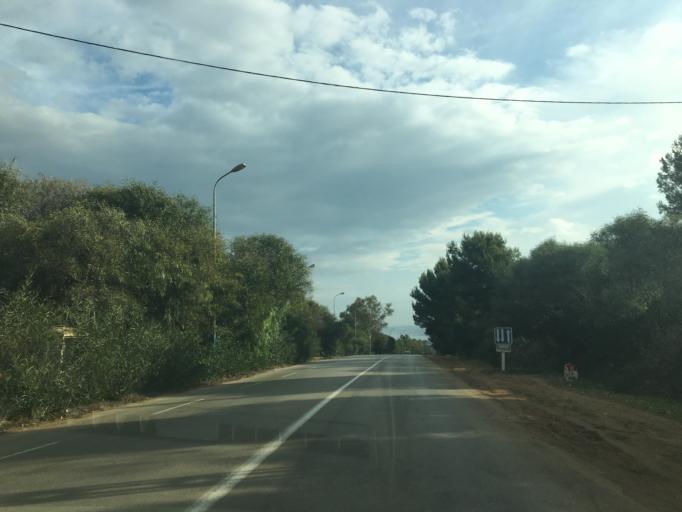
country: DZ
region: Tipaza
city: Tipasa
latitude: 36.5890
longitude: 2.4784
